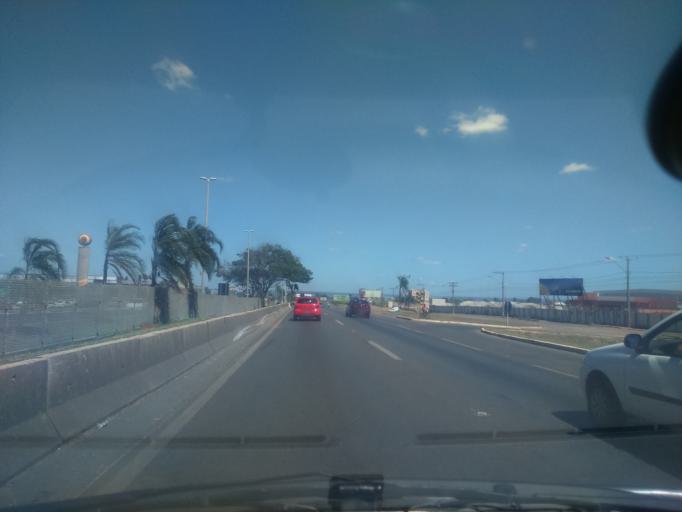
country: BR
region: Goias
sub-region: Luziania
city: Luziania
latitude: -16.0789
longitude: -47.9861
